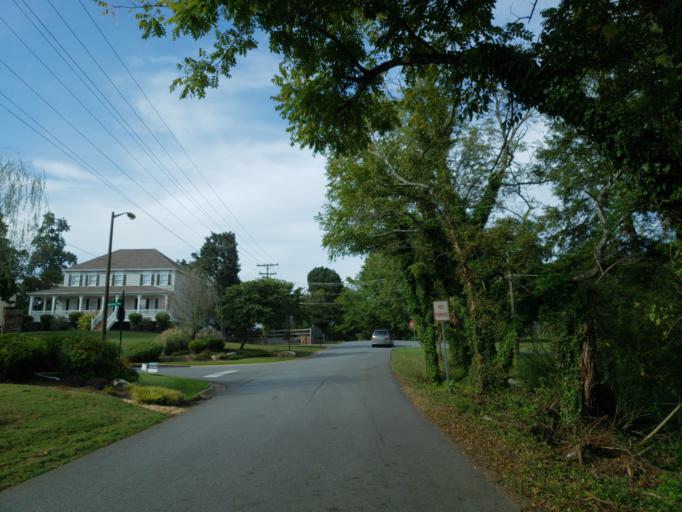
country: US
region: Georgia
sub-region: Cherokee County
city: Woodstock
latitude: 34.0801
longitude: -84.4979
